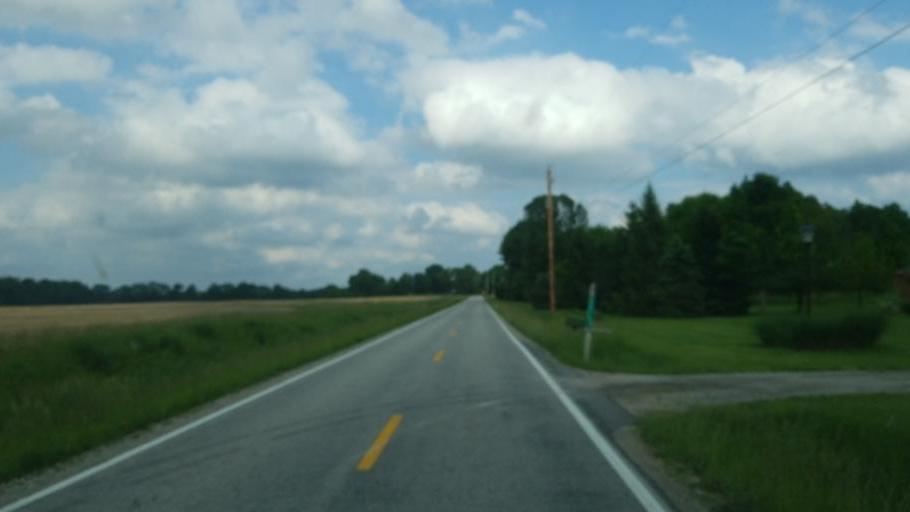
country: US
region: Ohio
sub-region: Delaware County
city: Sunbury
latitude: 40.2165
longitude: -82.8393
